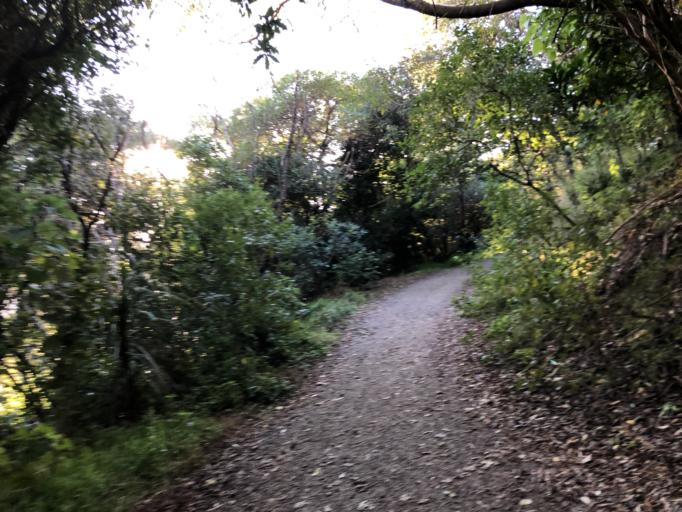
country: NZ
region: Wellington
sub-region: Wellington City
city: Wellington
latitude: -41.2975
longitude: 174.7907
